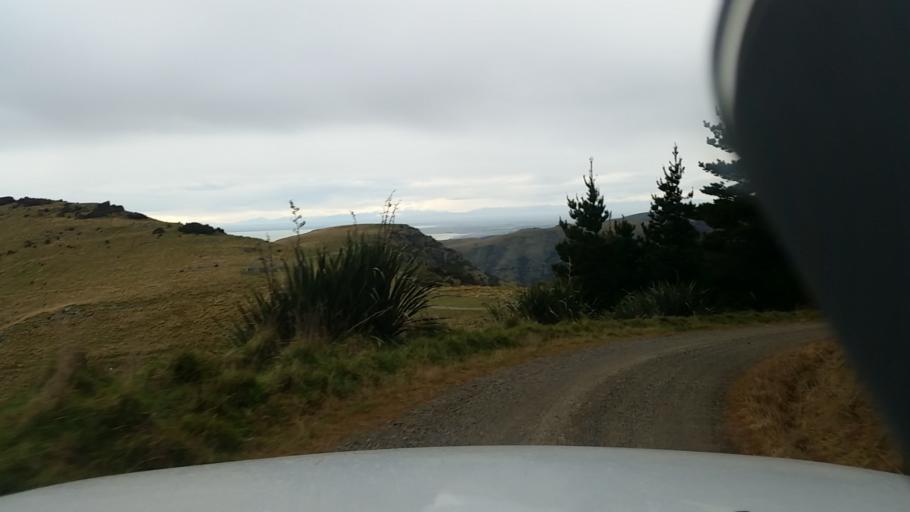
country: NZ
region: Canterbury
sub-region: Christchurch City
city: Christchurch
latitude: -43.8167
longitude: 172.7684
